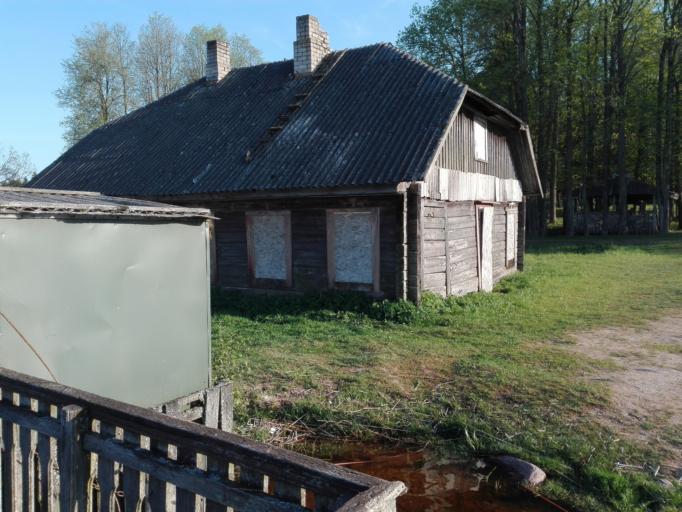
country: LT
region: Vilnius County
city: Ukmerge
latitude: 55.4264
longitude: 24.5635
